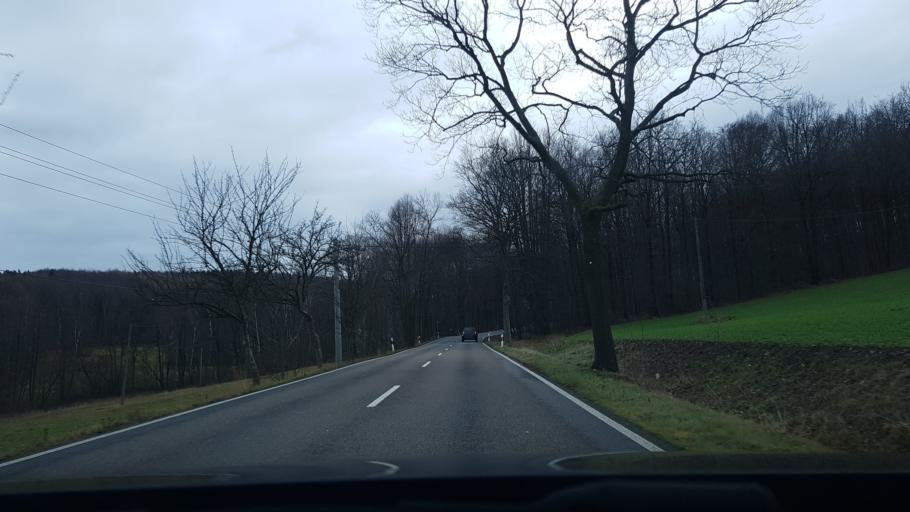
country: DE
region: Saxony
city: Dohma
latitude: 50.8659
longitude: 13.9564
